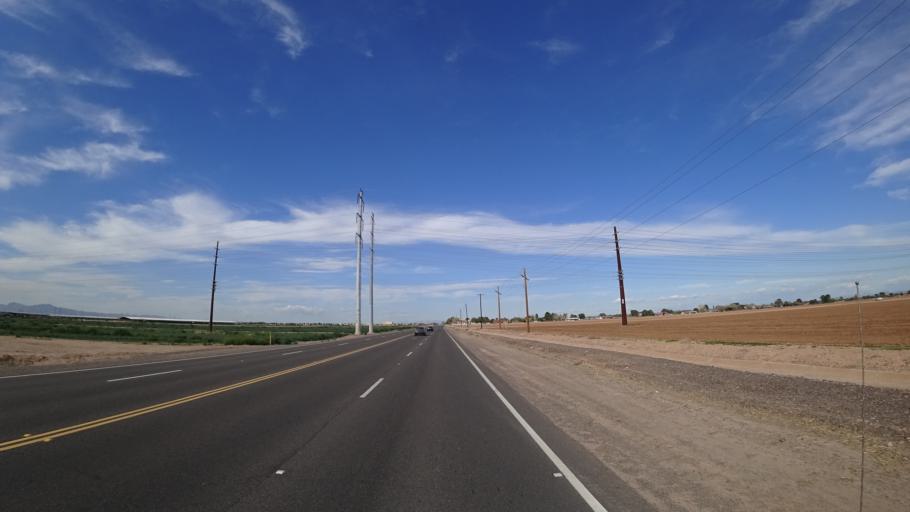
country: US
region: Arizona
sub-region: Maricopa County
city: Avondale
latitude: 33.4124
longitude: -112.3062
